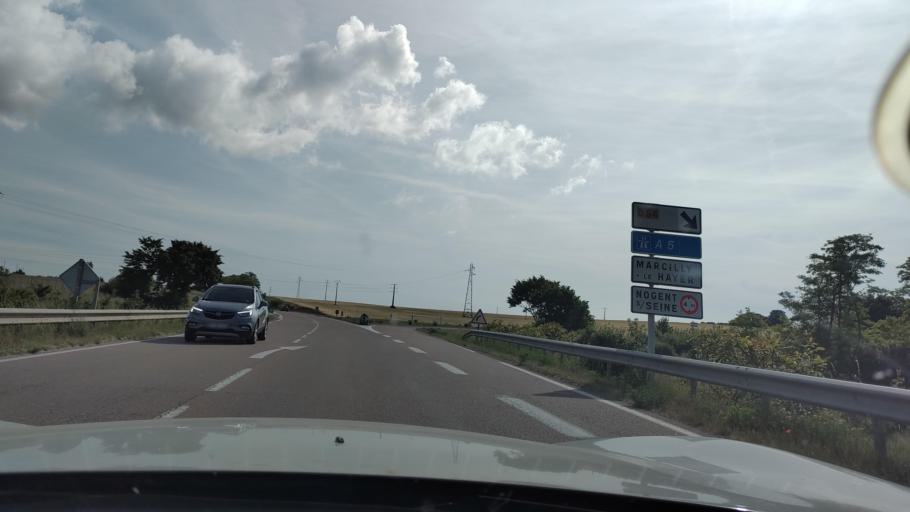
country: FR
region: Champagne-Ardenne
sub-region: Departement de l'Aube
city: Nogent-sur-Seine
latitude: 48.4842
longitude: 3.5137
